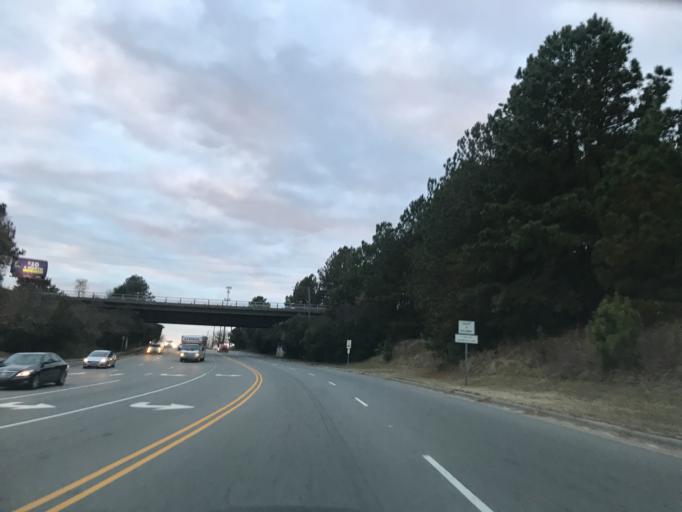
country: US
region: North Carolina
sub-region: Wake County
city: Raleigh
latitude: 35.8173
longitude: -78.6167
